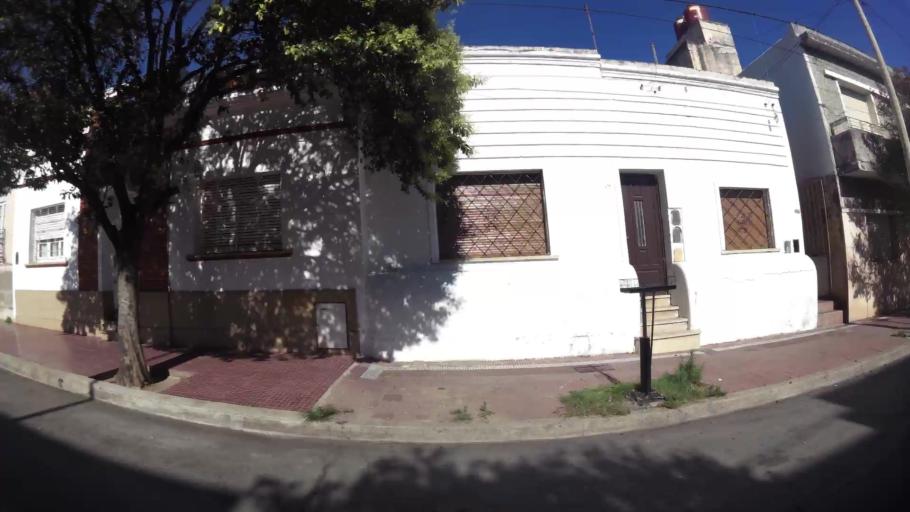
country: AR
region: Cordoba
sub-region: Departamento de Capital
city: Cordoba
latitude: -31.4252
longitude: -64.1622
